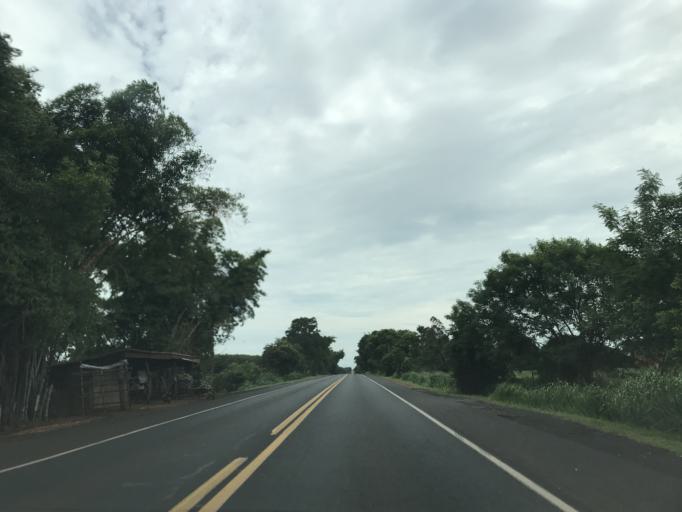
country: BR
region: Minas Gerais
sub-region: Frutal
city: Frutal
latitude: -20.1688
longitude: -49.1132
